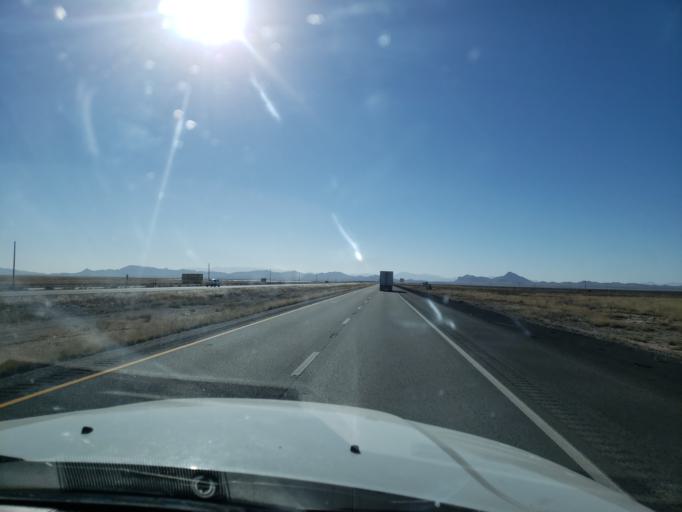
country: US
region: New Mexico
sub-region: Hidalgo County
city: Lordsburg
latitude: 32.2965
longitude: -108.8524
